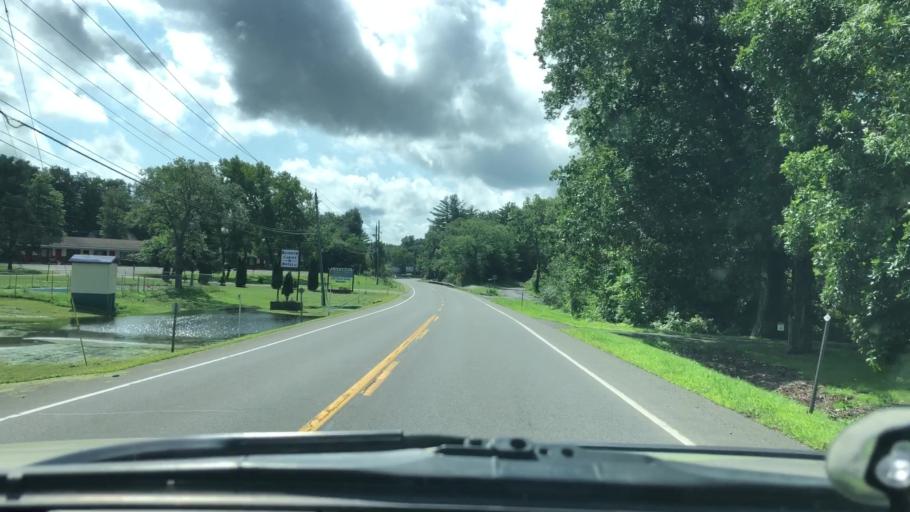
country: US
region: New York
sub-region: Greene County
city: Palenville
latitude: 42.2112
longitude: -73.9849
